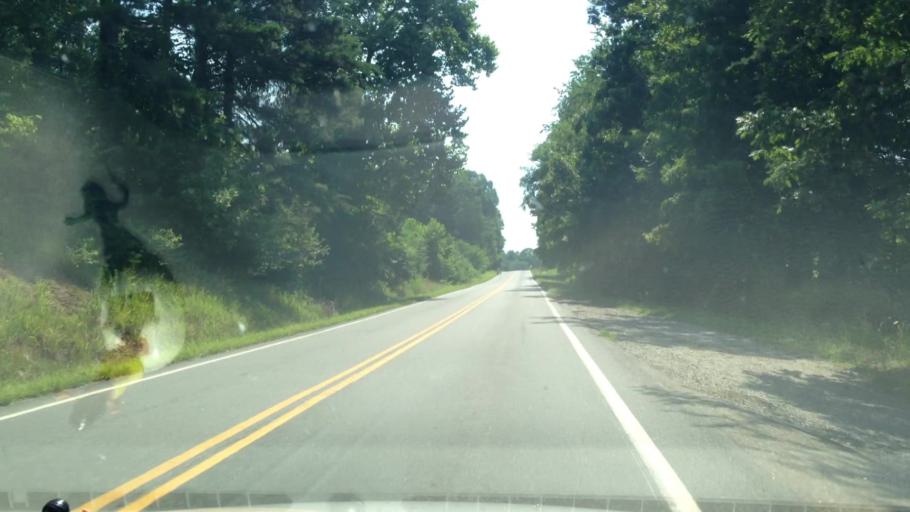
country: US
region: Virginia
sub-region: Patrick County
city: Stuart
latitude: 36.5783
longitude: -80.3701
